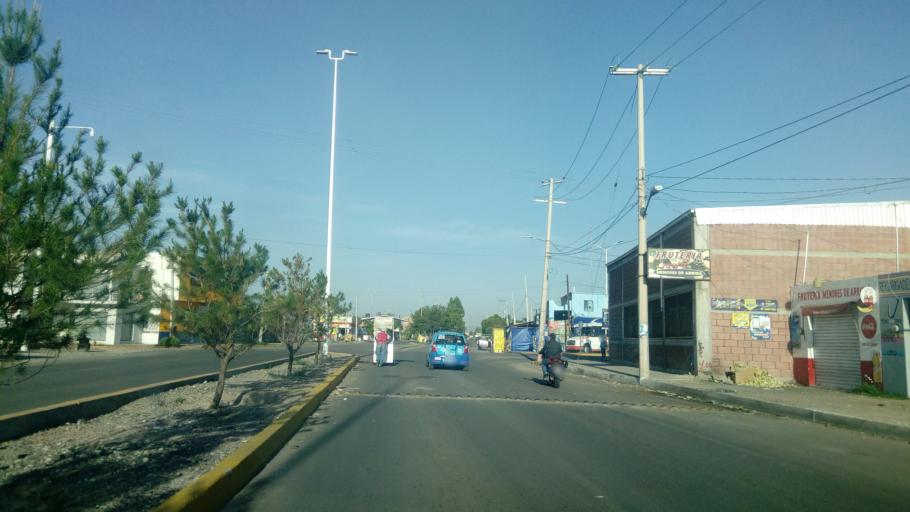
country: MX
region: Durango
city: Victoria de Durango
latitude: 24.0565
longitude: -104.5889
